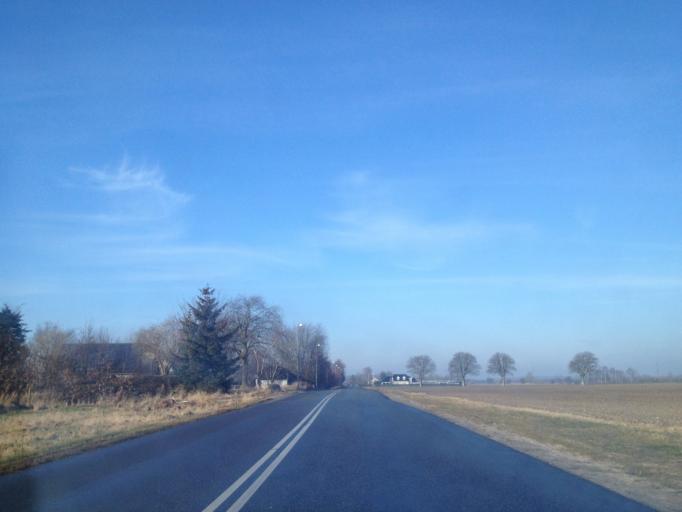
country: DK
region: Zealand
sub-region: Greve Kommune
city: Greve
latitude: 55.6061
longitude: 12.2897
